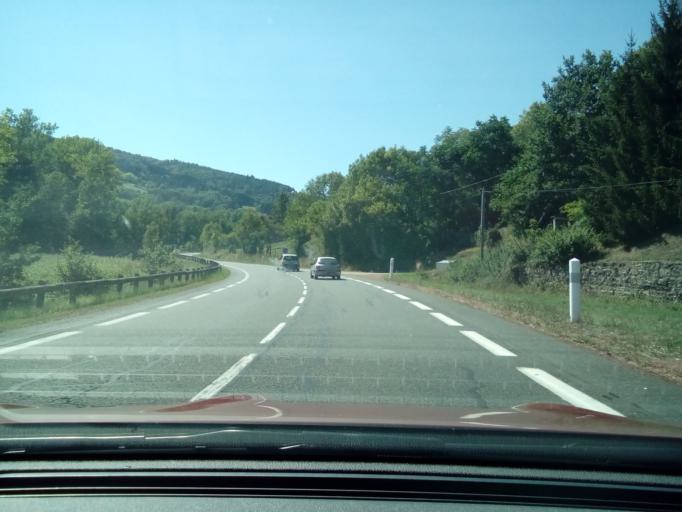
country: FR
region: Rhone-Alpes
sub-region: Departement du Rhone
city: Pontcharra-sur-Turdine
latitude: 45.9229
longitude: 4.4775
